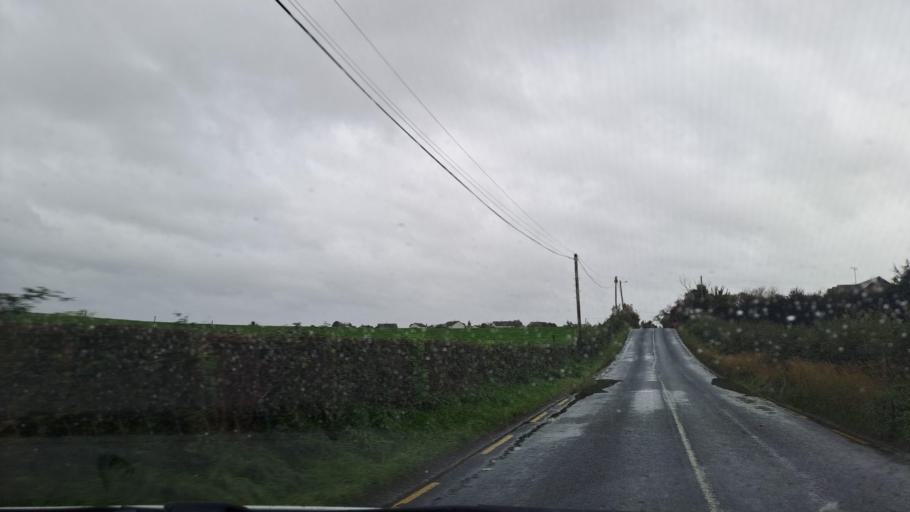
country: IE
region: Leinster
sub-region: Lu
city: Dundalk
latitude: 53.9785
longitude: -6.4919
